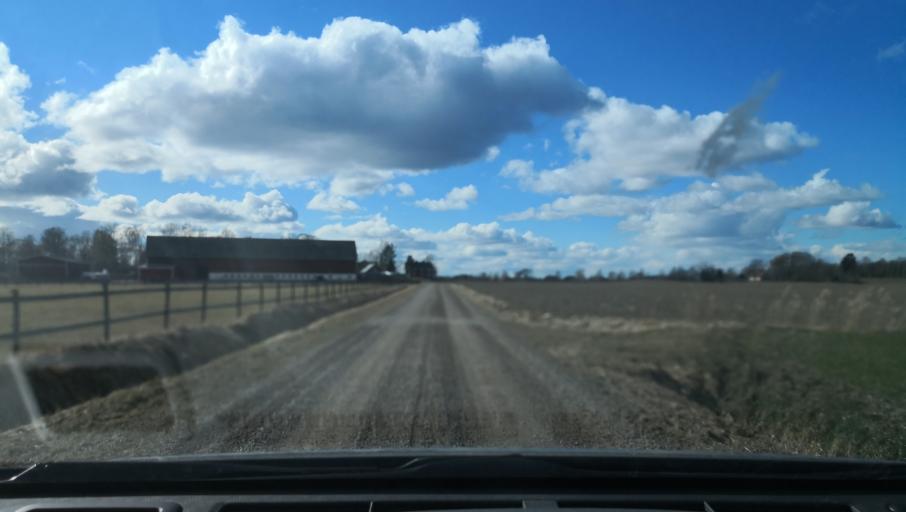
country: SE
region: OErebro
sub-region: Lindesbergs Kommun
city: Fellingsbro
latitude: 59.4139
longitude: 15.6435
